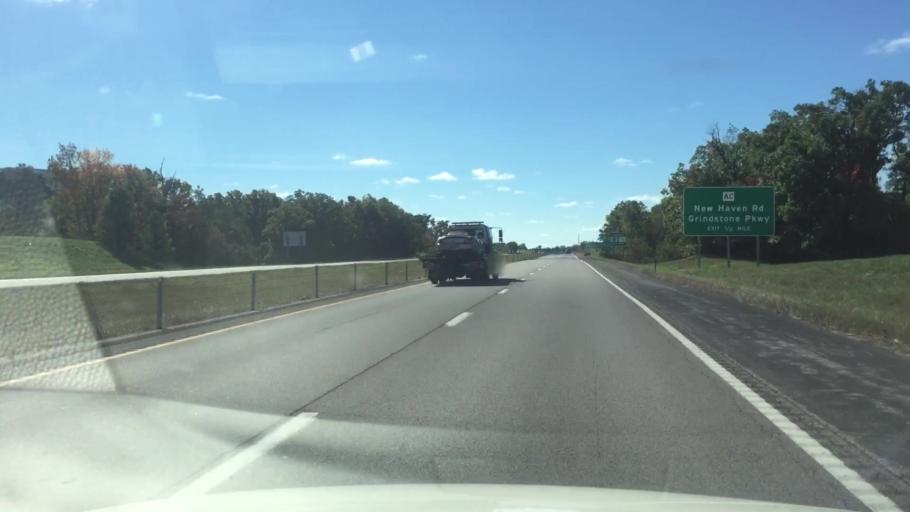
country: US
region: Missouri
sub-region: Boone County
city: Columbia
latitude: 38.9237
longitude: -92.2946
